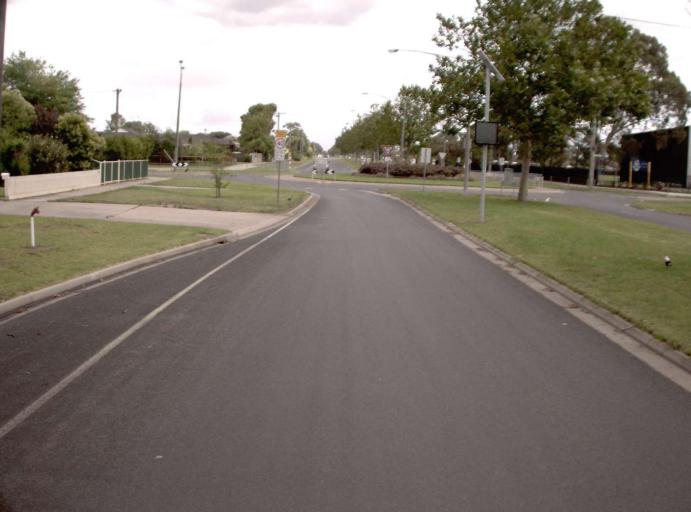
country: AU
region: Victoria
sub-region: Wellington
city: Sale
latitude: -38.1005
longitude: 147.0844
